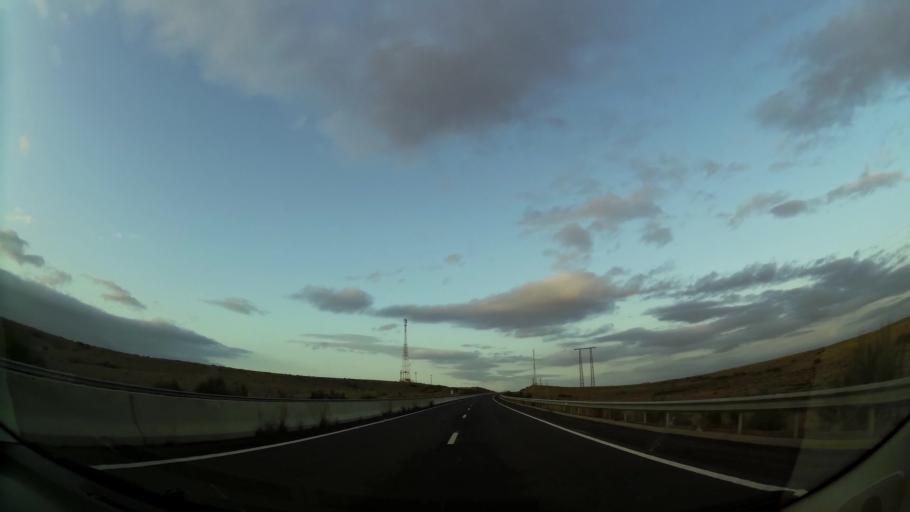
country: MA
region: Oriental
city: Taourirt
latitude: 34.5461
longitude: -2.9021
